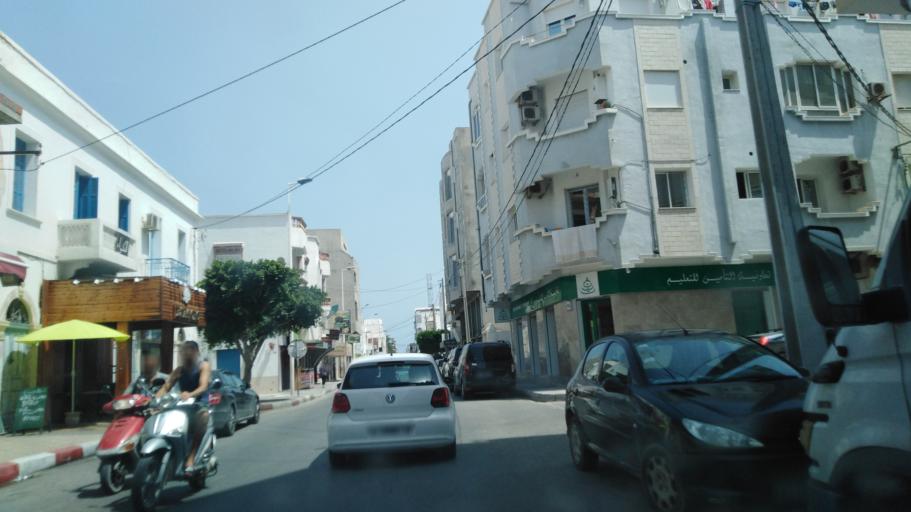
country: TN
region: Al Mahdiyah
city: Mahdia
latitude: 35.5084
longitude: 11.0545
